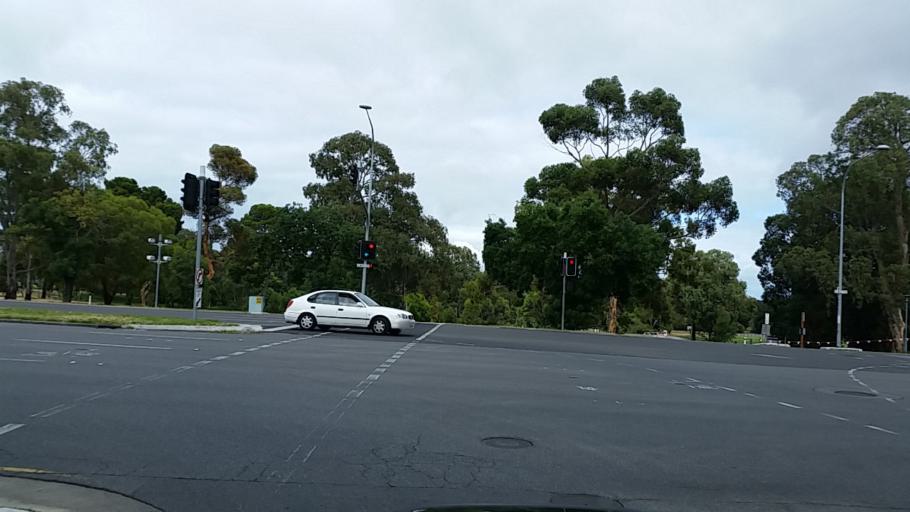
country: AU
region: South Australia
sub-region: Adelaide
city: Adelaide
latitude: -34.9236
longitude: 138.5877
